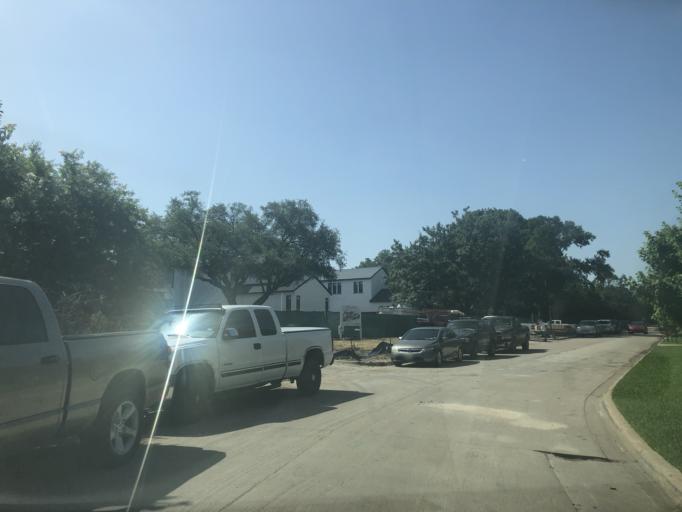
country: US
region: Texas
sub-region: Dallas County
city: University Park
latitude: 32.8822
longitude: -96.8139
